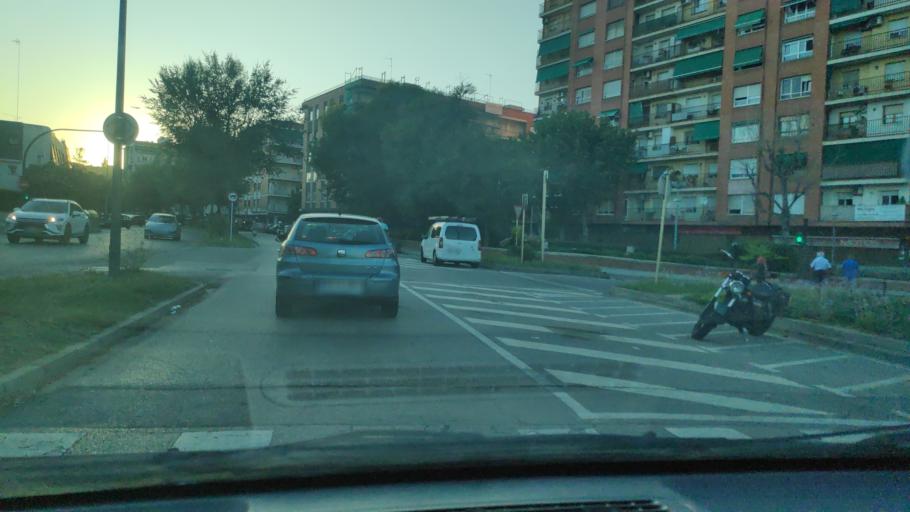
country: ES
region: Catalonia
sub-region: Provincia de Barcelona
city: Ripollet
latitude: 41.4891
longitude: 2.1511
